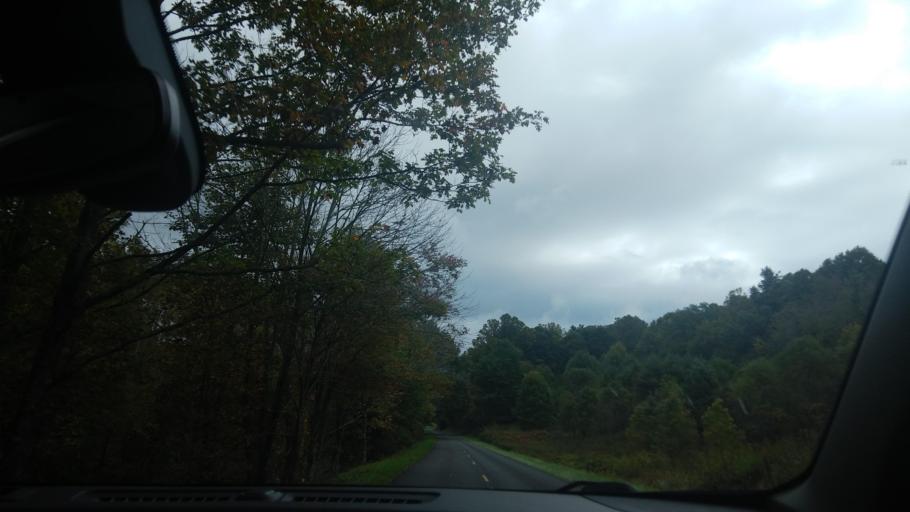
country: US
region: Virginia
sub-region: Carroll County
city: Cana
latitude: 36.6553
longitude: -80.5624
